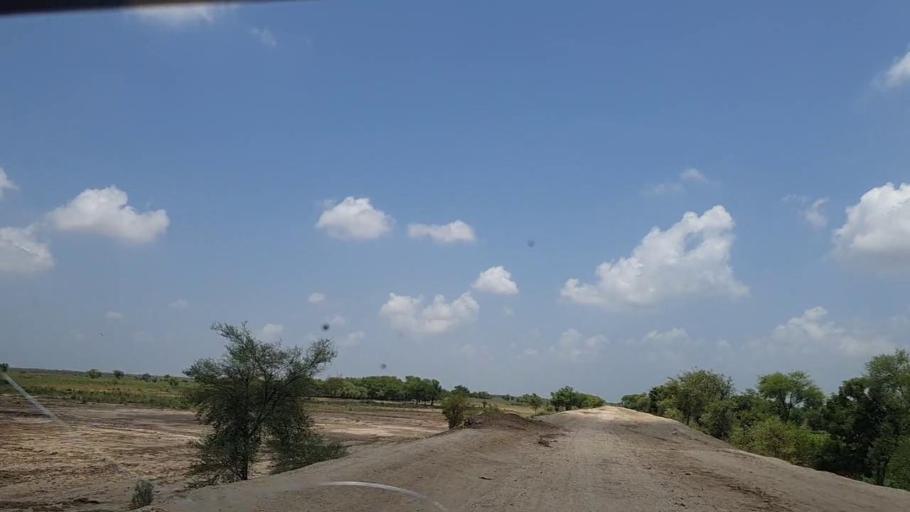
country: PK
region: Sindh
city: Tharu Shah
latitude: 26.9310
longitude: 67.9908
